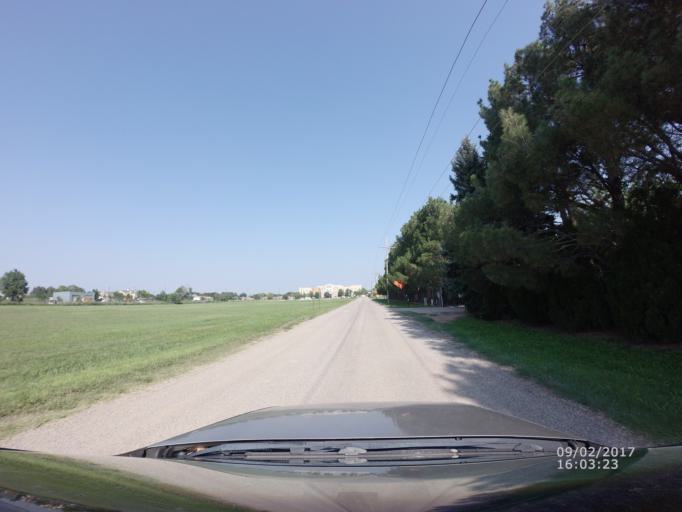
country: US
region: New Mexico
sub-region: Curry County
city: Clovis
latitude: 34.4423
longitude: -103.1996
